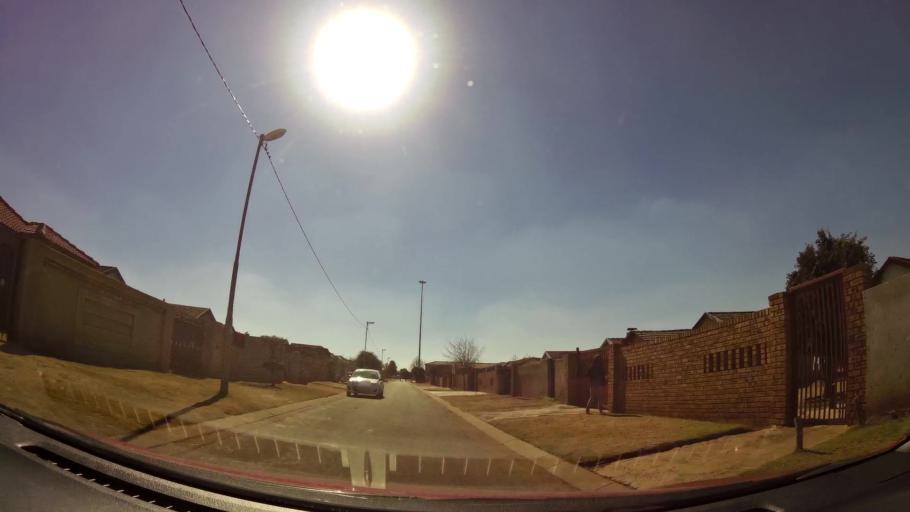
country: ZA
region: Gauteng
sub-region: City of Johannesburg Metropolitan Municipality
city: Soweto
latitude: -26.2453
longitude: 27.8058
